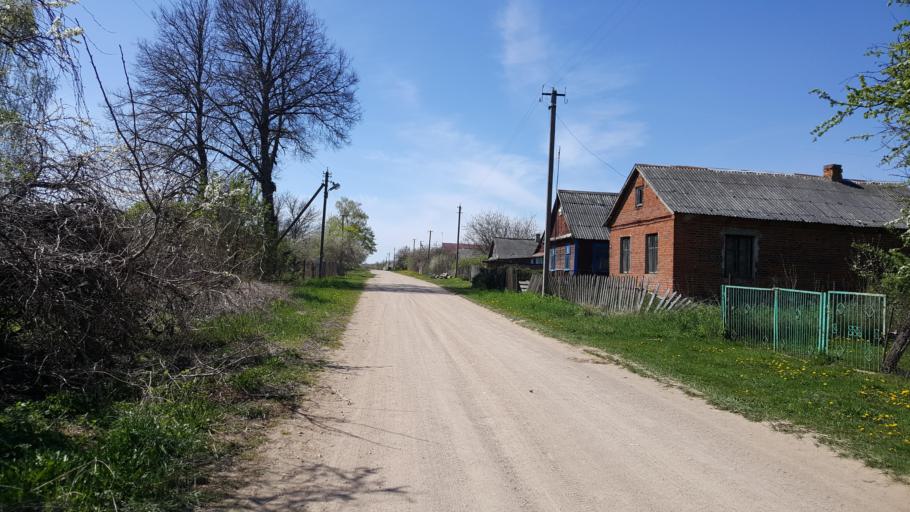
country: BY
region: Brest
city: Vysokaye
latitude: 52.3519
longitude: 23.4504
